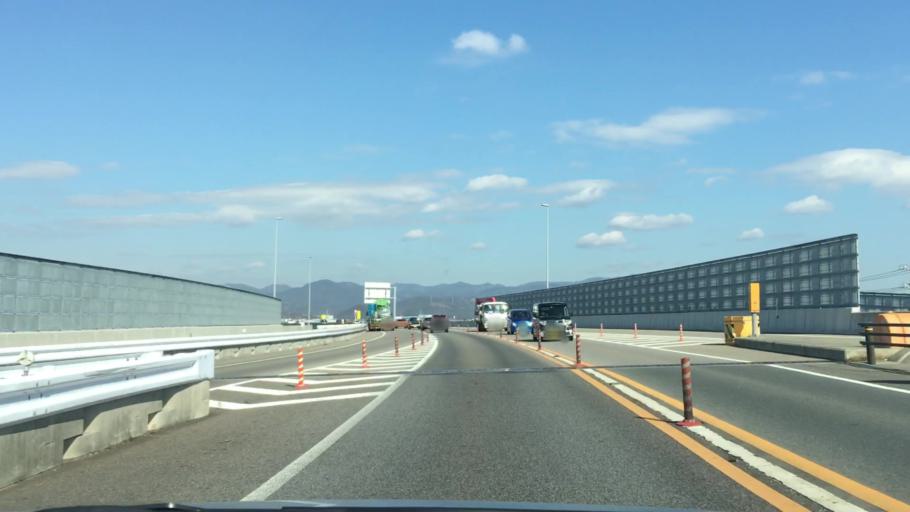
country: JP
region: Aichi
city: Kozakai-cho
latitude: 34.8038
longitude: 137.3371
